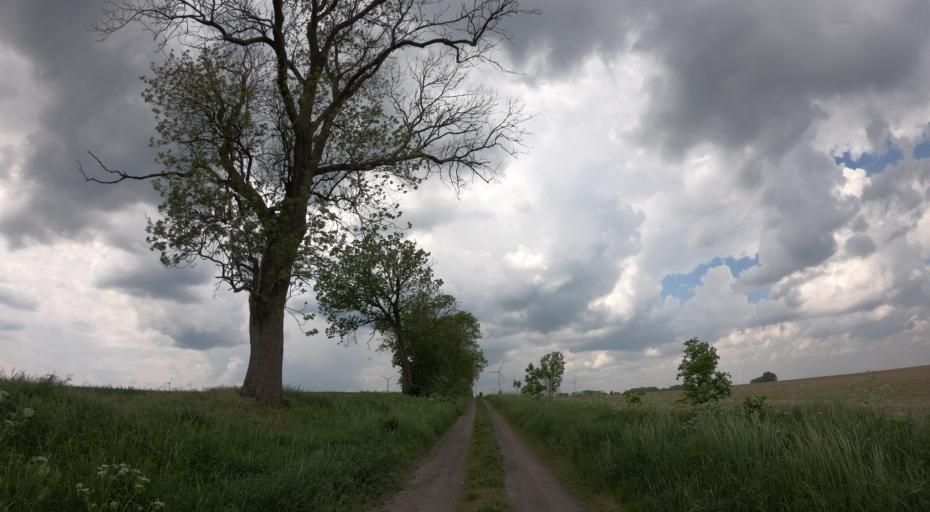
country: PL
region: West Pomeranian Voivodeship
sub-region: Powiat pyrzycki
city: Pyrzyce
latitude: 53.1043
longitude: 14.8712
